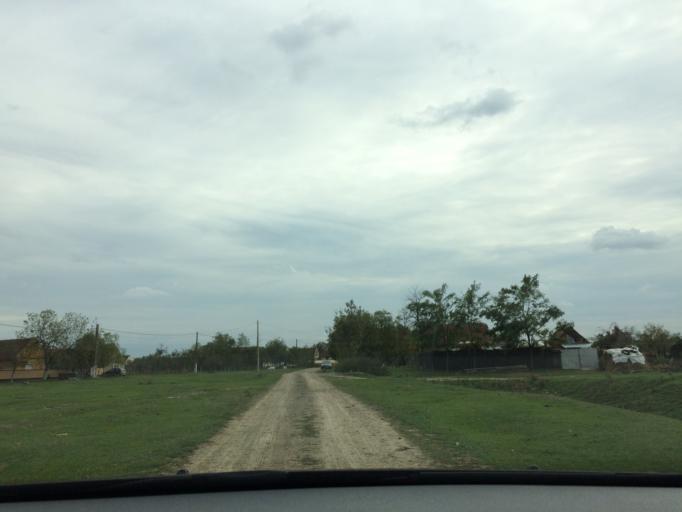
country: RO
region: Timis
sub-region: Oras Recas
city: Recas
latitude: 45.7442
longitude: 21.4888
